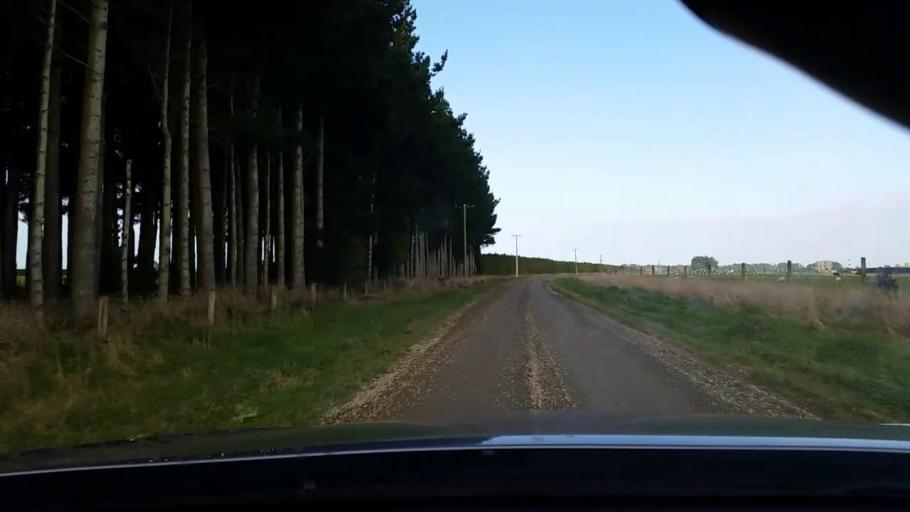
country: NZ
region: Southland
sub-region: Invercargill City
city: Invercargill
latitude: -46.2815
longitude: 168.2943
